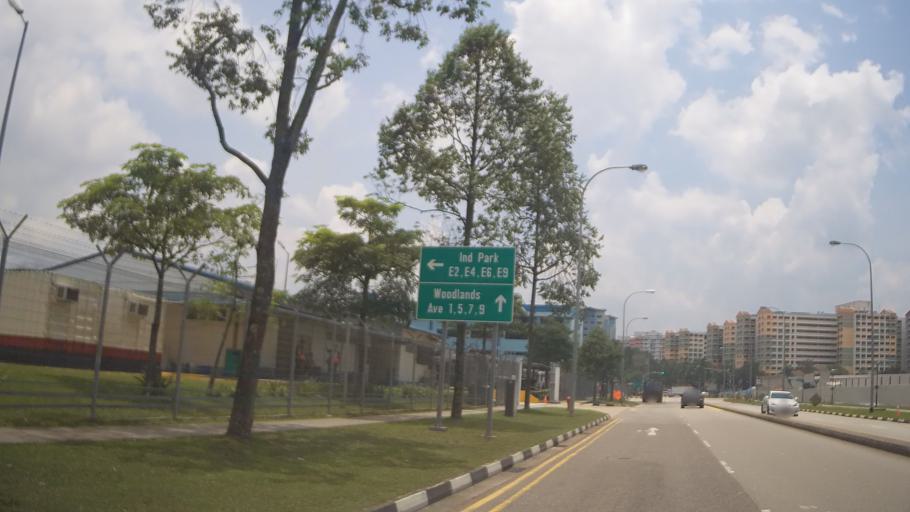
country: MY
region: Johor
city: Johor Bahru
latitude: 1.4491
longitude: 103.7915
